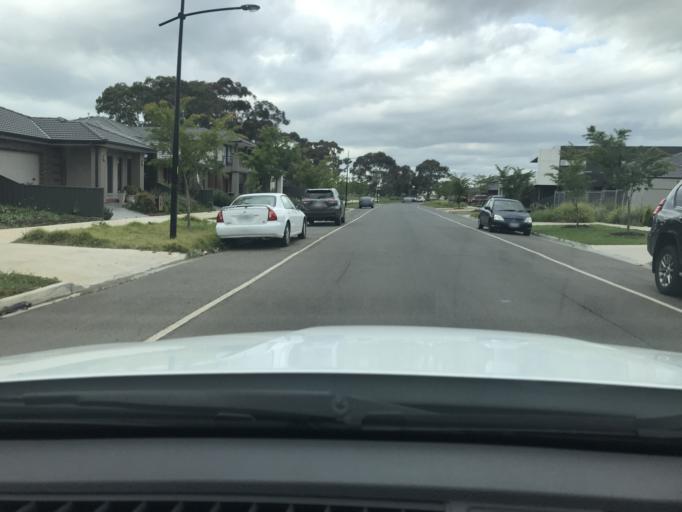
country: AU
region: Victoria
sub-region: Hume
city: Greenvale
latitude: -37.5938
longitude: 144.8879
